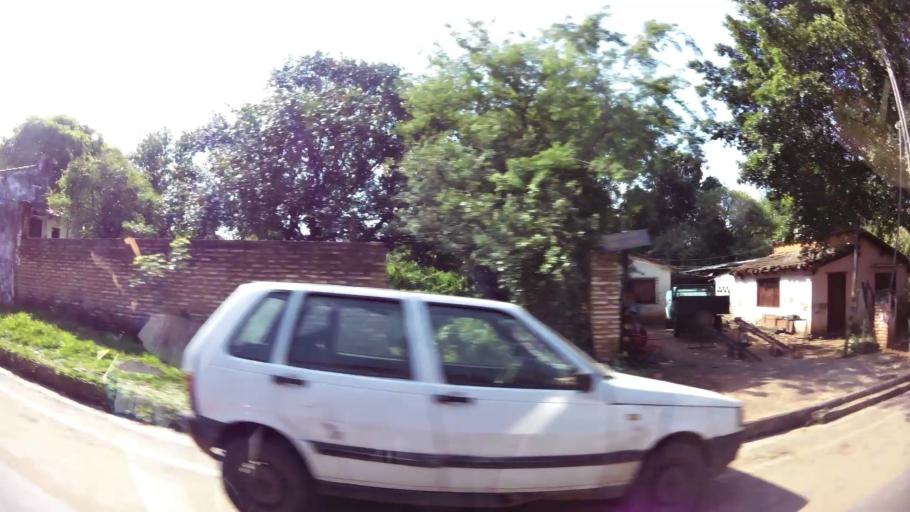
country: PY
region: Central
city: San Lorenzo
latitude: -25.3512
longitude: -57.5048
